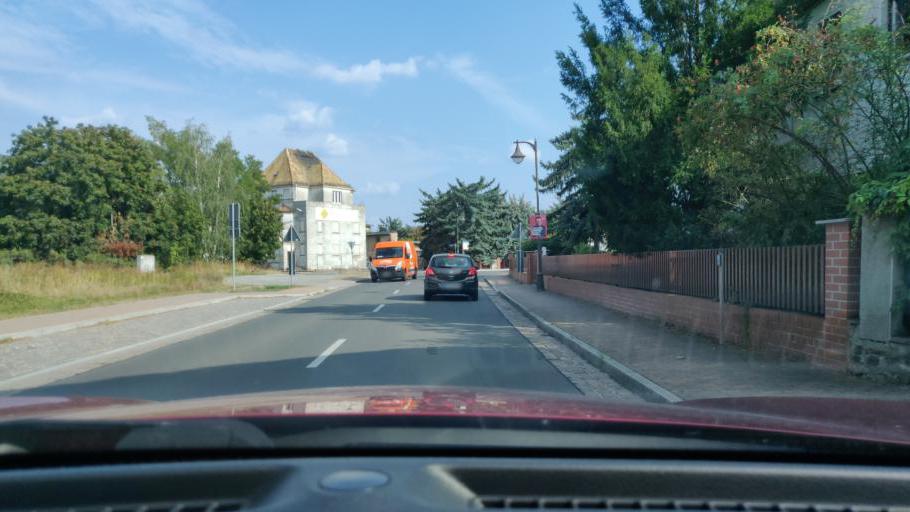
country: DE
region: Saxony
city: Mockrehna
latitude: 51.5045
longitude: 12.8176
